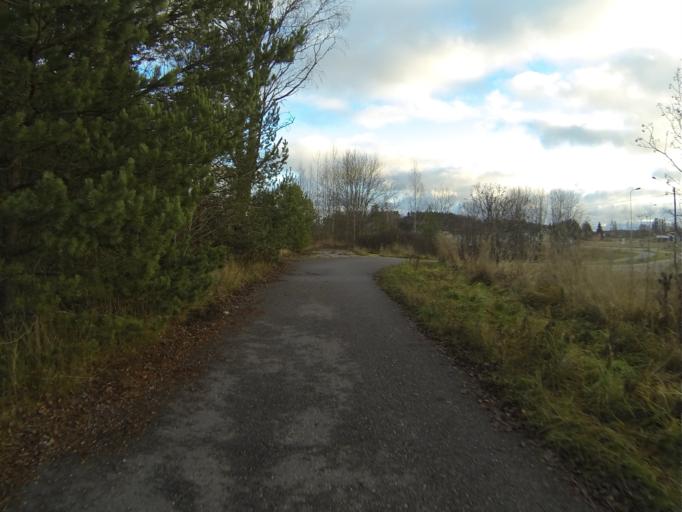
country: FI
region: Varsinais-Suomi
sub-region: Salo
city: Halikko
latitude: 60.3990
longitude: 23.0423
